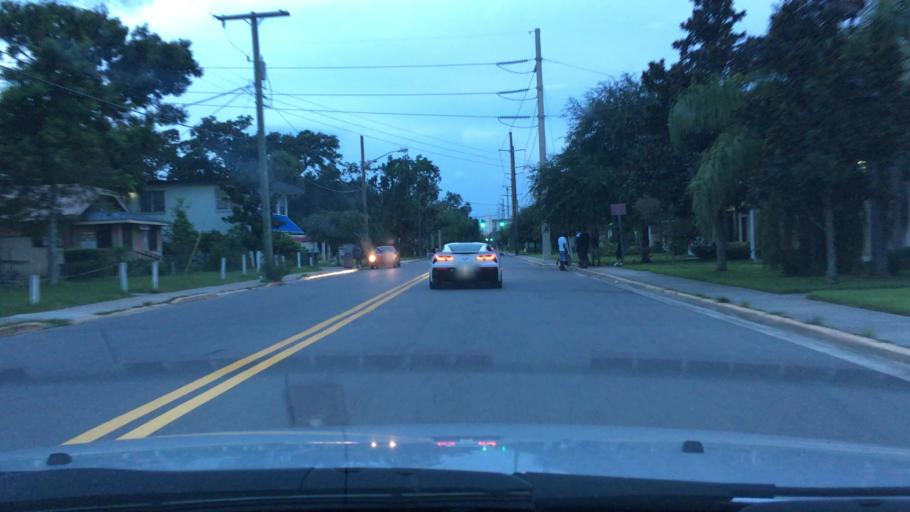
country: US
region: Florida
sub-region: Volusia County
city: Daytona Beach
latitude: 29.2089
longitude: -81.0373
